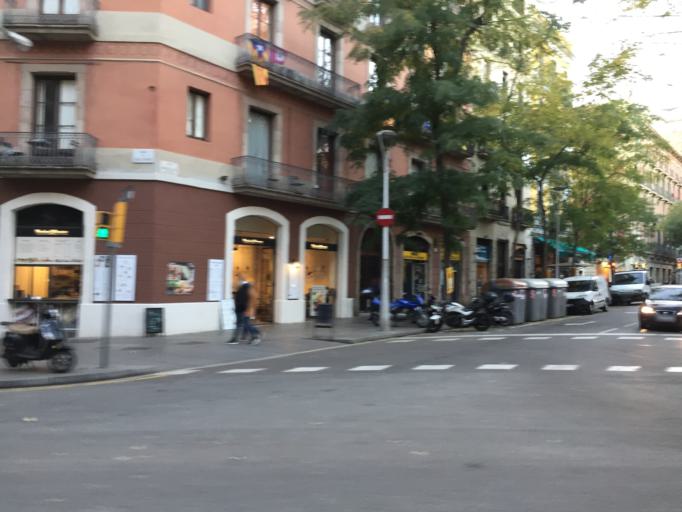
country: ES
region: Catalonia
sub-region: Provincia de Barcelona
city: Eixample
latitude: 41.3833
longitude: 2.1635
